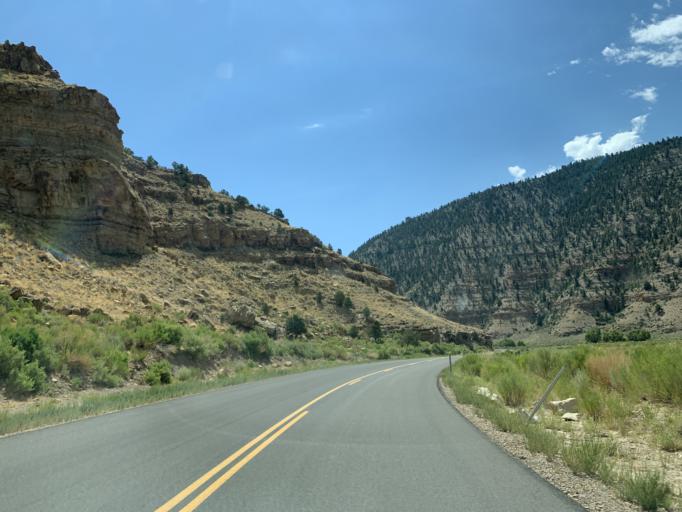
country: US
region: Utah
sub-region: Carbon County
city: East Carbon City
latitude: 39.8039
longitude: -110.3721
